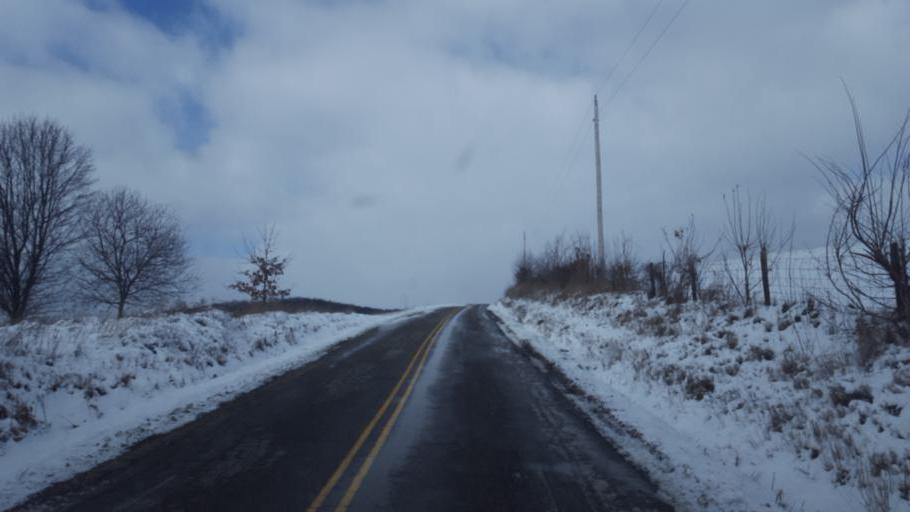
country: US
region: Ohio
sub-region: Knox County
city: Danville
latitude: 40.4993
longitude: -82.3561
